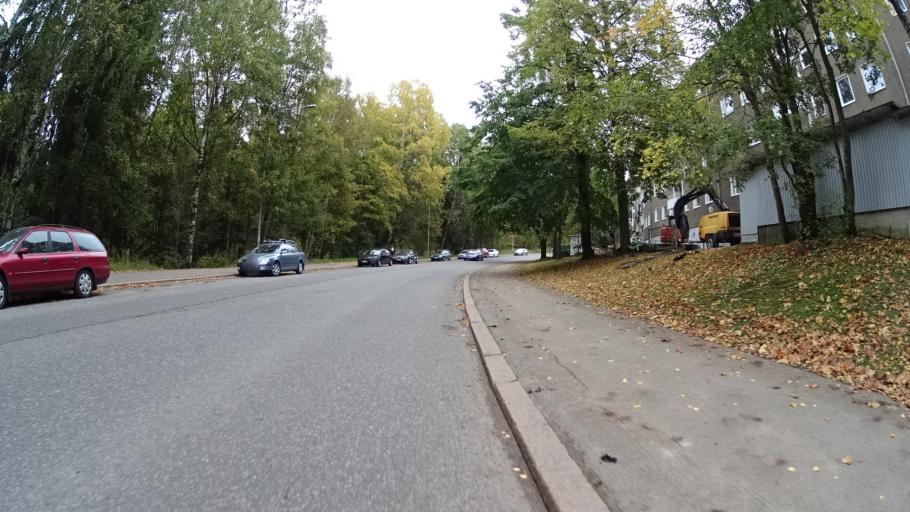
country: FI
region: Uusimaa
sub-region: Helsinki
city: Teekkarikylae
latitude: 60.2100
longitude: 24.8702
